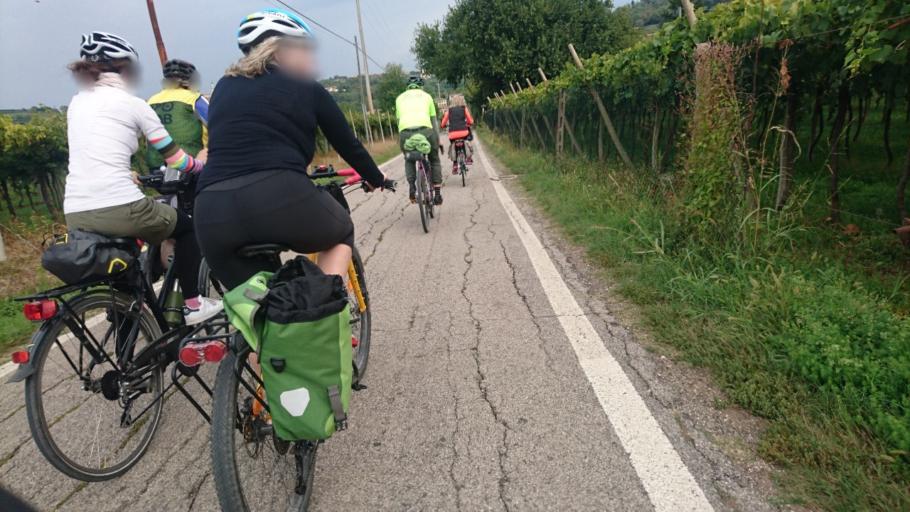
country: IT
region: Veneto
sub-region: Provincia di Verona
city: Colognola ai Colli
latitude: 45.4187
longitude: 11.1967
